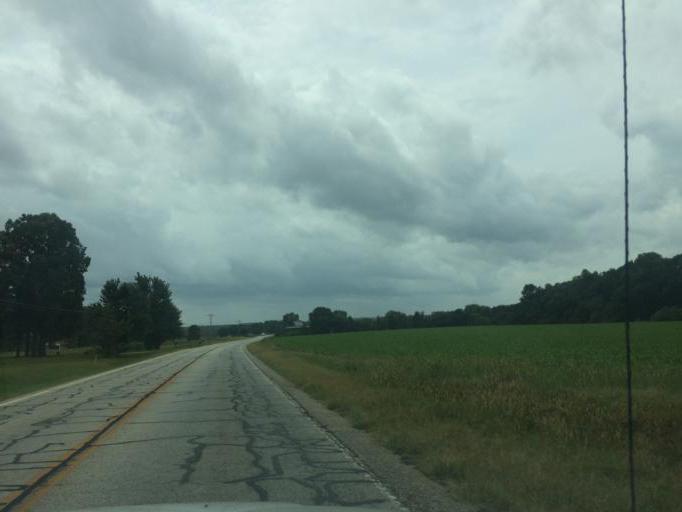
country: US
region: Georgia
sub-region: Hart County
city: Hartwell
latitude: 34.2616
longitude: -82.8964
